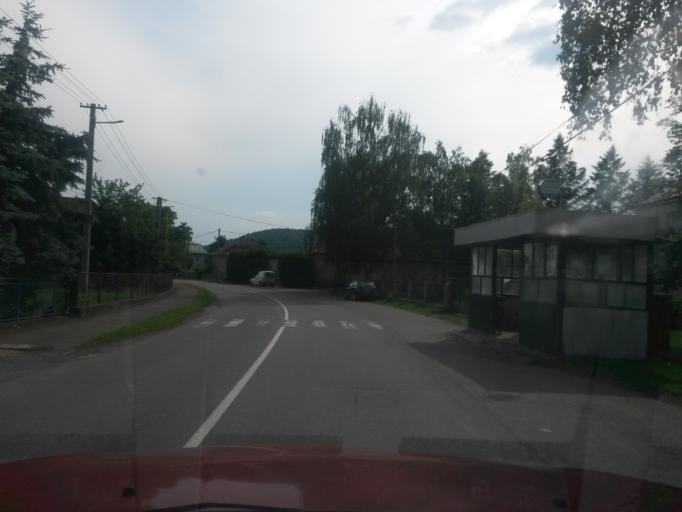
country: SK
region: Presovsky
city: Humenne
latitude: 48.9949
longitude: 22.0132
